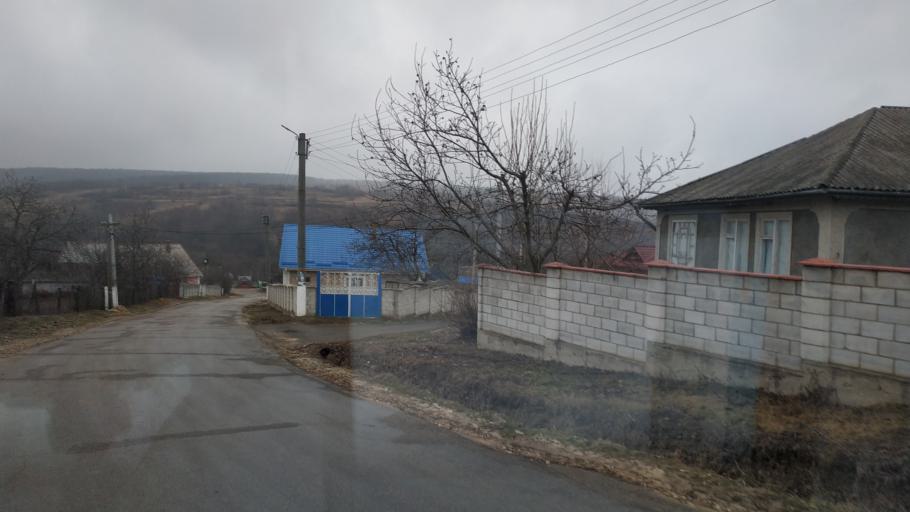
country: MD
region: Laloveni
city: Ialoveni
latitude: 46.8889
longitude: 28.6887
